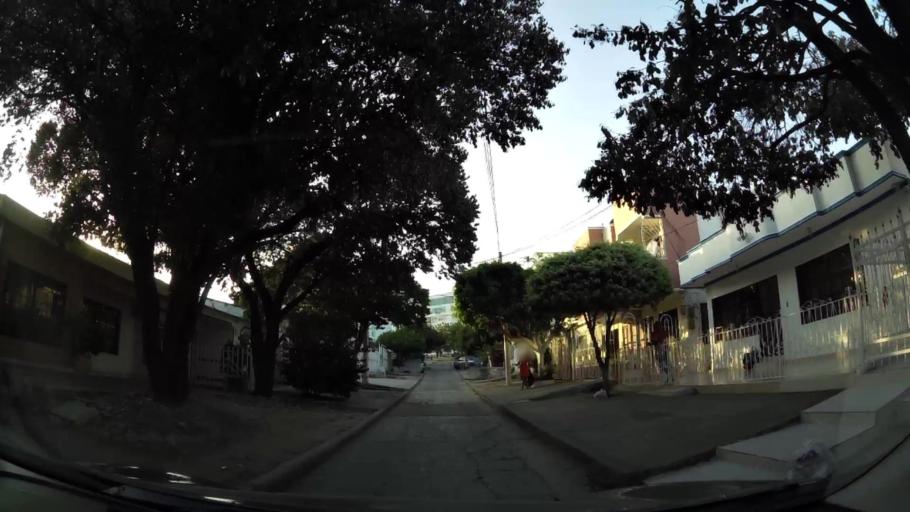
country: CO
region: Bolivar
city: Cartagena
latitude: 10.3911
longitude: -75.4858
